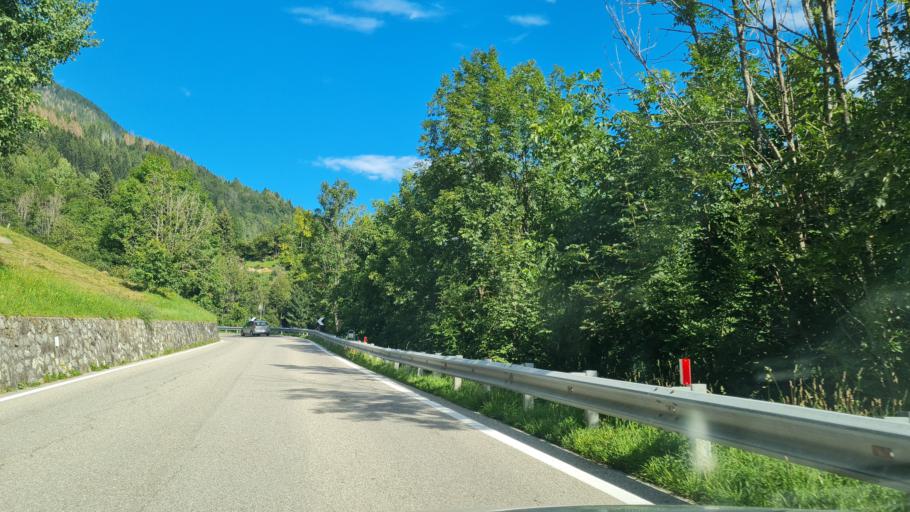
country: IT
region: Trentino-Alto Adige
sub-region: Provincia di Trento
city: Siror
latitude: 46.1929
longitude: 11.8246
